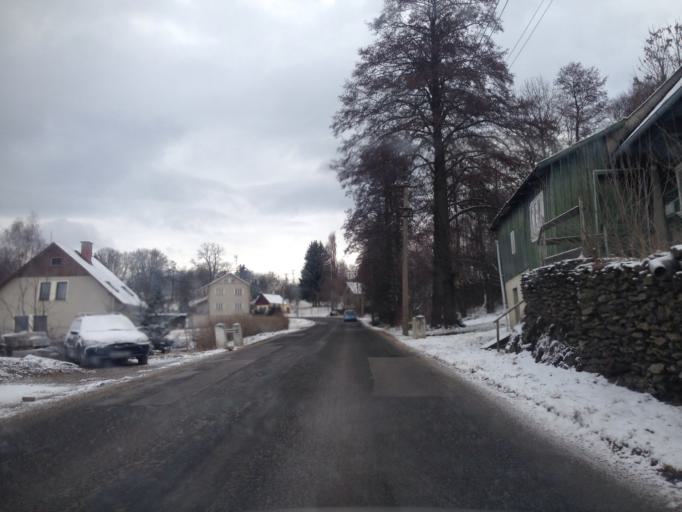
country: CZ
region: Liberecky
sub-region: Okres Semily
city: Vysoke nad Jizerou
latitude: 50.6622
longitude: 15.4164
